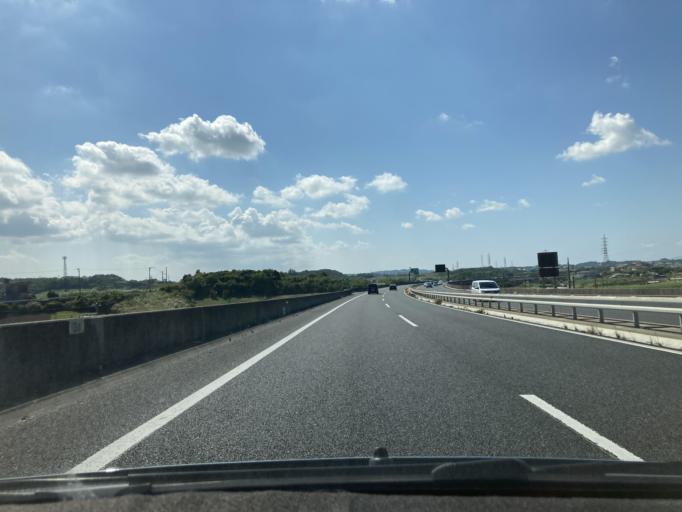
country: JP
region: Okinawa
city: Tomigusuku
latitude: 26.1881
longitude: 127.7379
